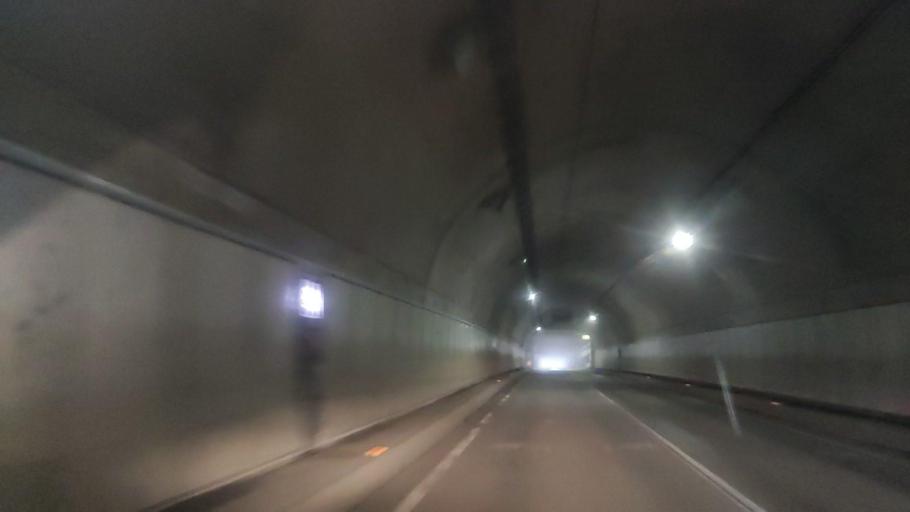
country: JP
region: Hokkaido
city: Date
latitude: 42.5519
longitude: 141.0803
